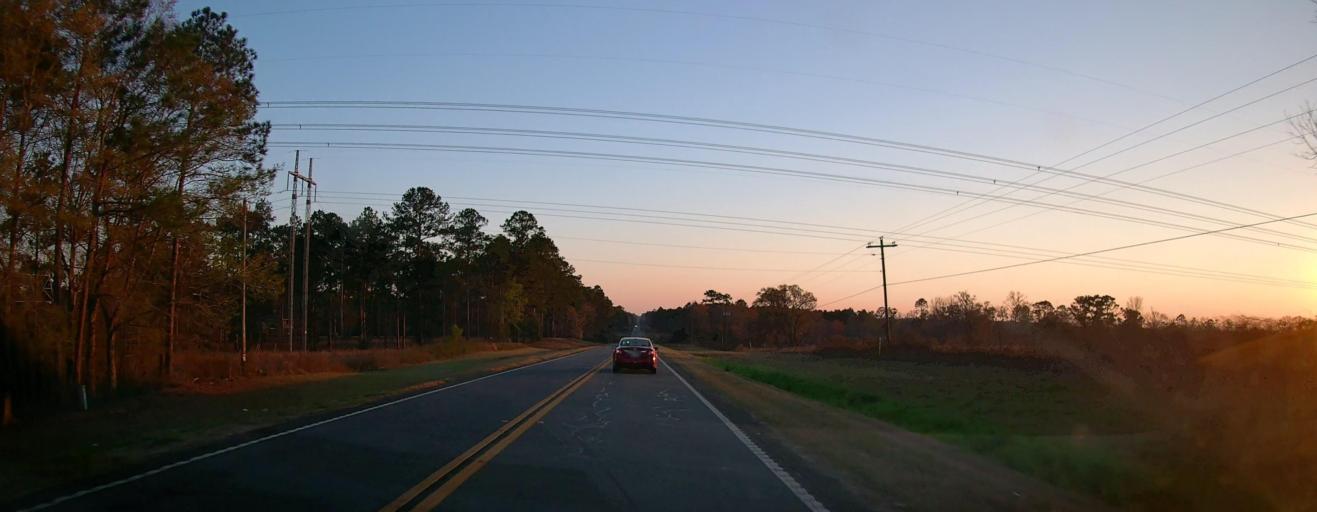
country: US
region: Georgia
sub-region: Dodge County
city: Eastman
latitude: 32.2494
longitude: -83.1427
